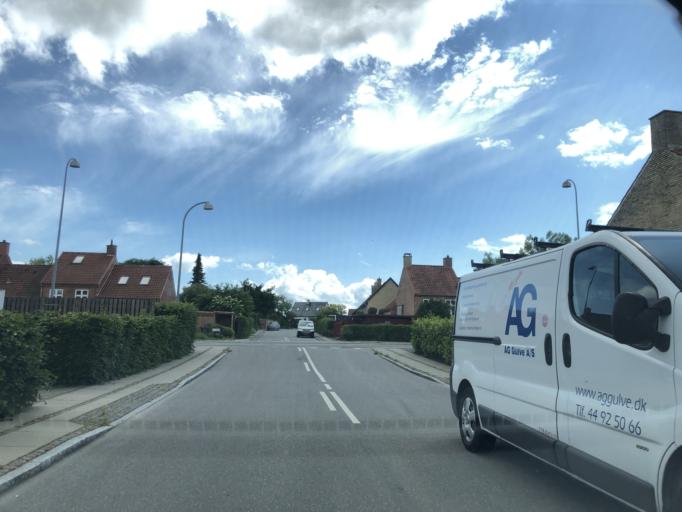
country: DK
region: Capital Region
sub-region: Hvidovre Kommune
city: Hvidovre
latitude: 55.6624
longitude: 12.4663
